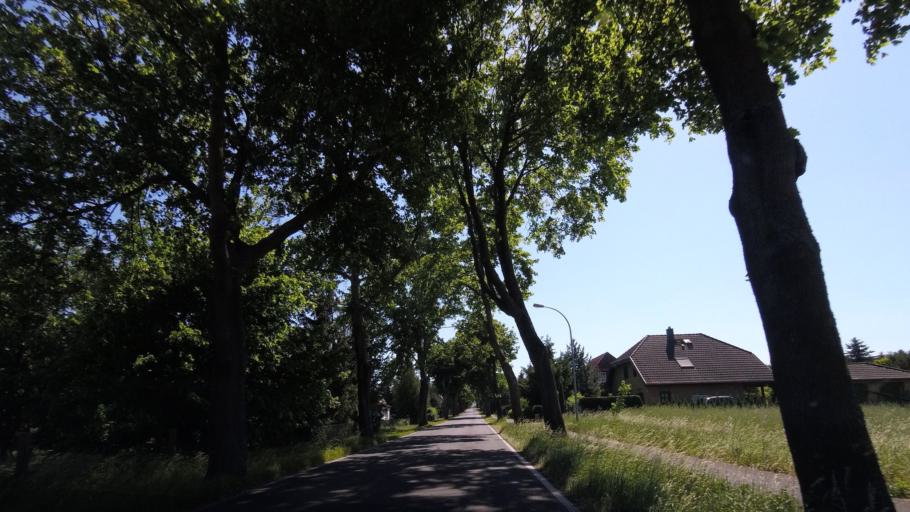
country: DE
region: Brandenburg
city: Gross Kreutz
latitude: 52.3973
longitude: 12.7127
